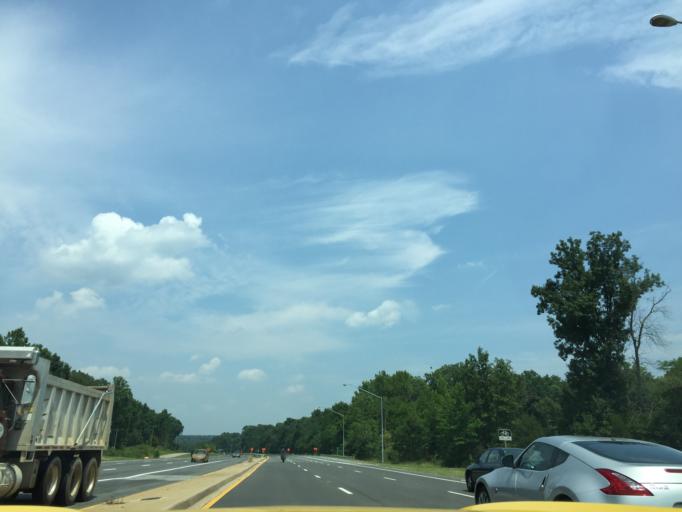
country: US
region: Maryland
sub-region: Prince George's County
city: Fort Washington
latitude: 38.6854
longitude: -76.9948
